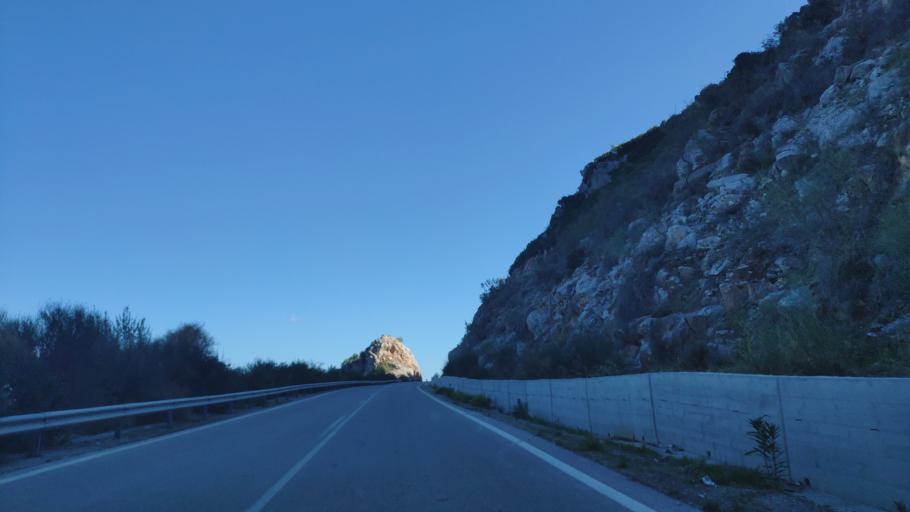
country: GR
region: Peloponnese
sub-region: Nomos Argolidos
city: Palaia Epidavros
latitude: 37.5855
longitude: 23.2250
